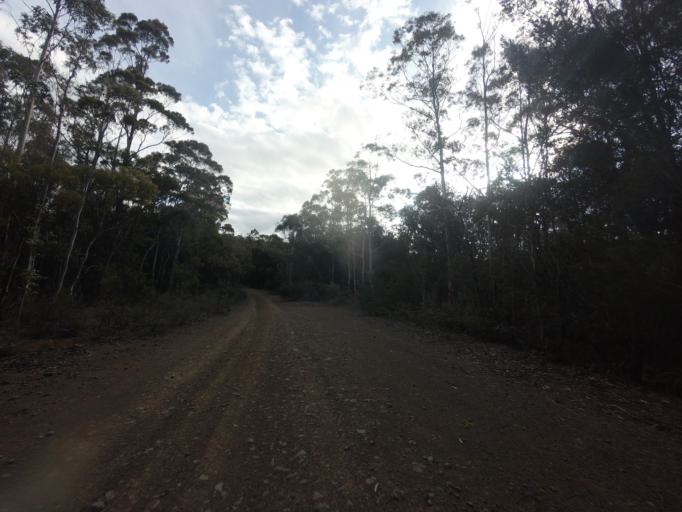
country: AU
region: Tasmania
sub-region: Break O'Day
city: St Helens
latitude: -41.8385
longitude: 148.0610
